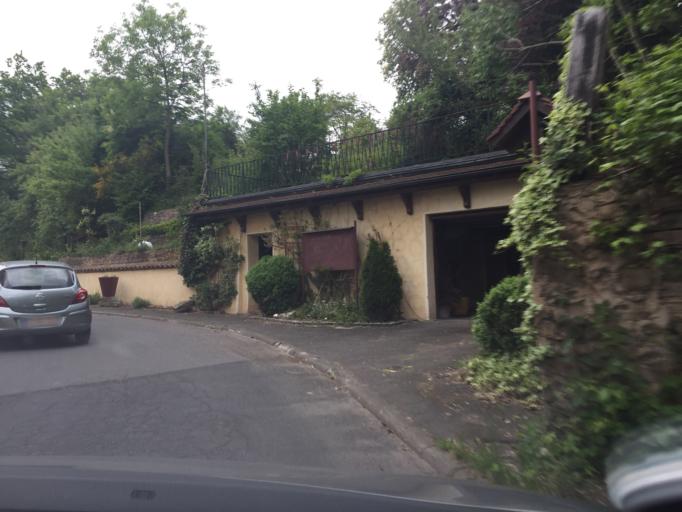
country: DE
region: Bavaria
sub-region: Regierungsbezirk Unterfranken
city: Johannesberg
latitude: 50.0401
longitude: 9.1112
